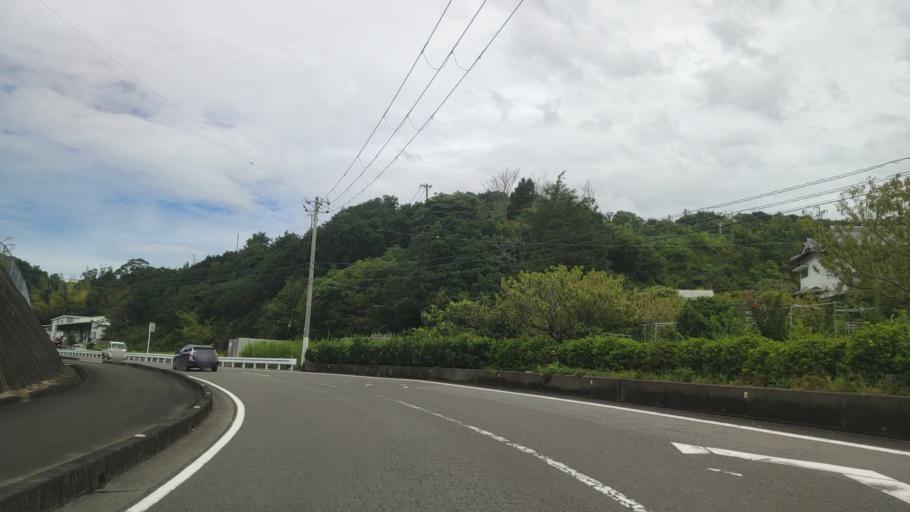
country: JP
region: Wakayama
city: Tanabe
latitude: 33.6826
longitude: 135.3890
